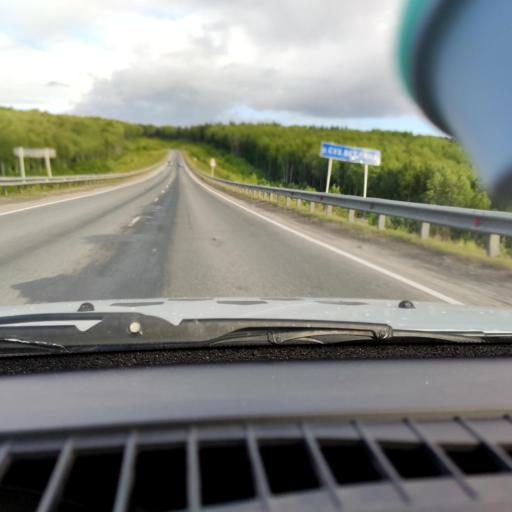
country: RU
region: Perm
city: Sylva
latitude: 58.2997
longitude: 56.7945
